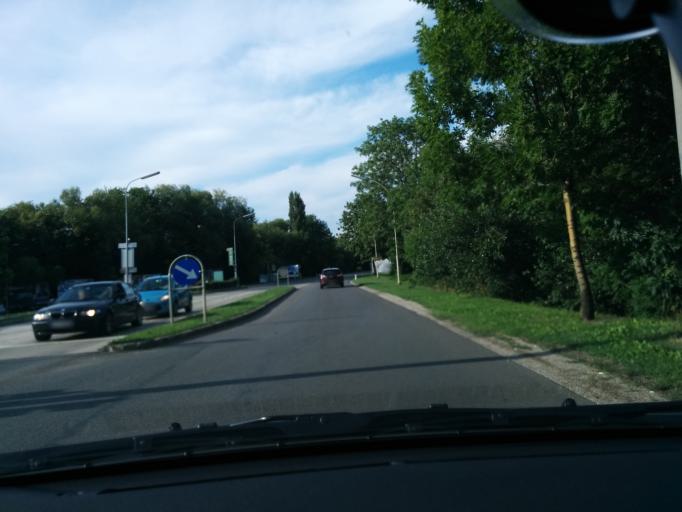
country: AT
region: Lower Austria
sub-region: Politischer Bezirk Baden
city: Gunselsdorf
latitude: 47.9450
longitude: 16.2606
